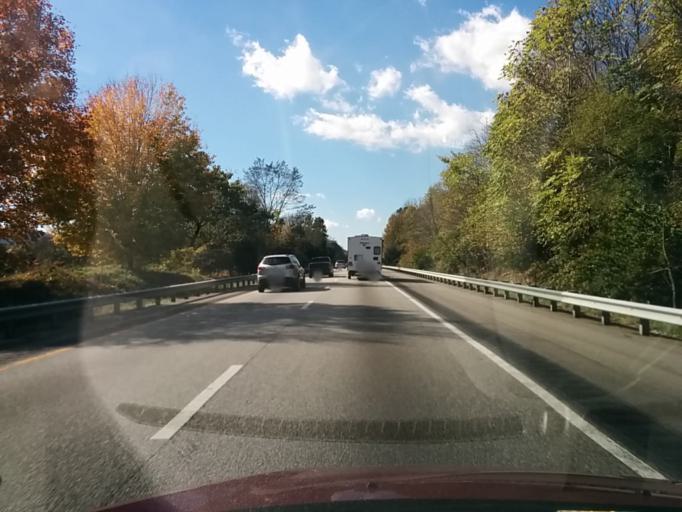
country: US
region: Virginia
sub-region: Botetourt County
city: Daleville
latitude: 37.4398
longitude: -79.8674
